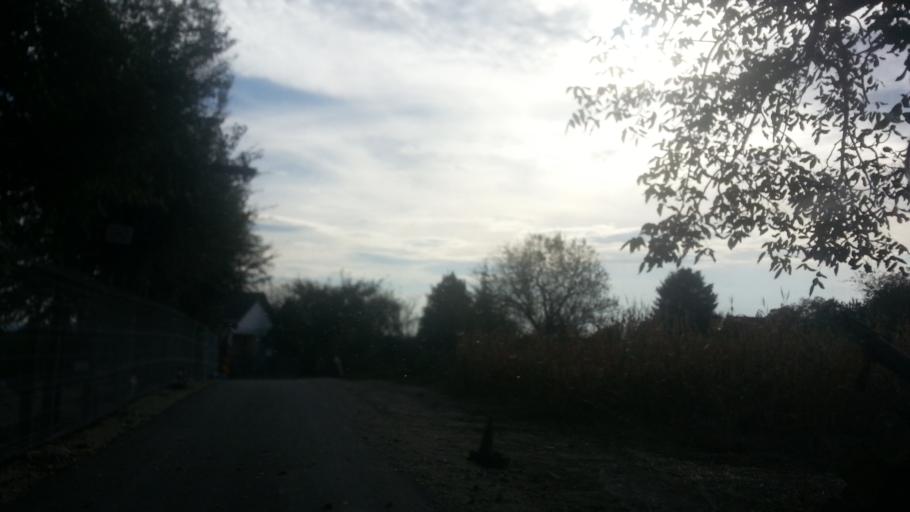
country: RS
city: Belegis
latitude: 45.0214
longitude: 20.3485
